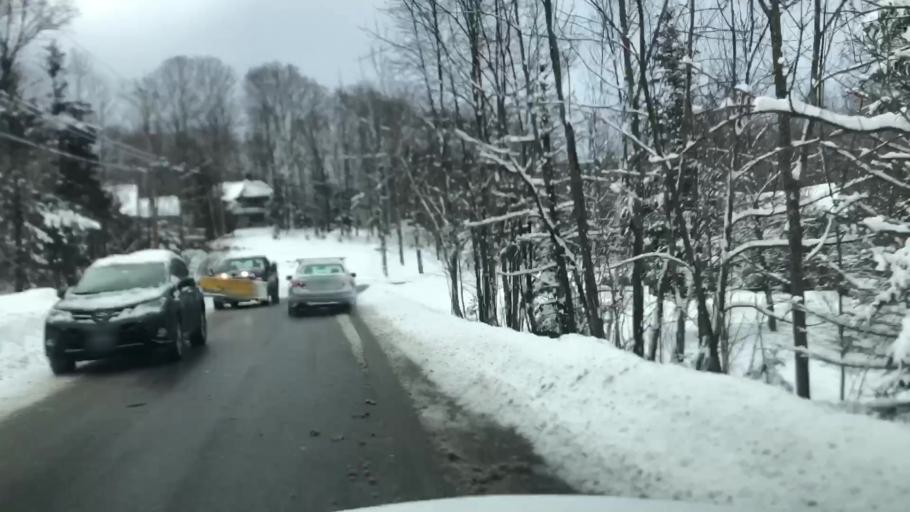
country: US
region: Vermont
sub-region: Rutland County
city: Rutland
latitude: 43.6476
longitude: -72.7865
